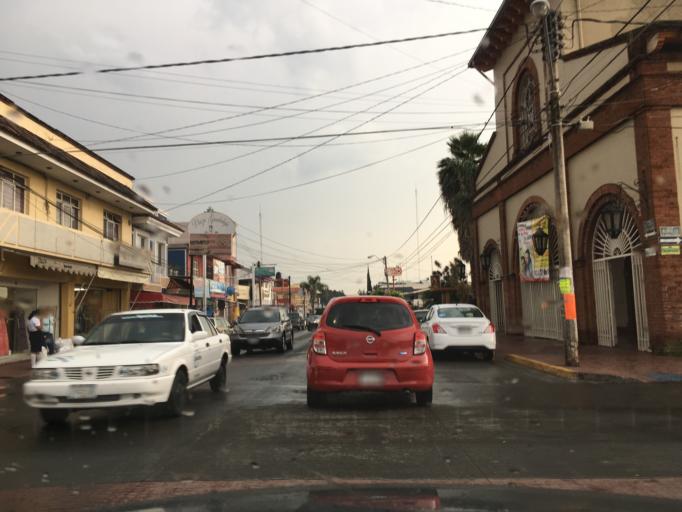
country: MX
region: Michoacan
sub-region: Uruapan
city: Uruapan
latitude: 19.4142
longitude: -102.0560
